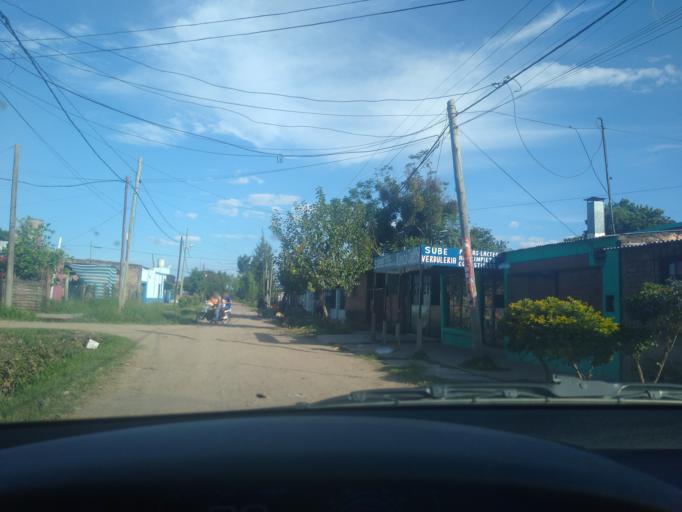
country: AR
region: Chaco
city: Barranqueras
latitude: -27.4695
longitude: -58.9327
